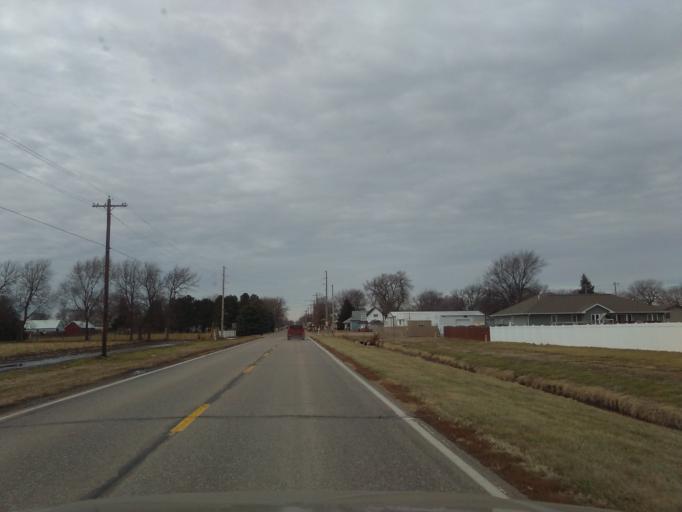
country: US
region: Nebraska
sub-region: Hall County
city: Grand Island
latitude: 40.7710
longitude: -98.3627
